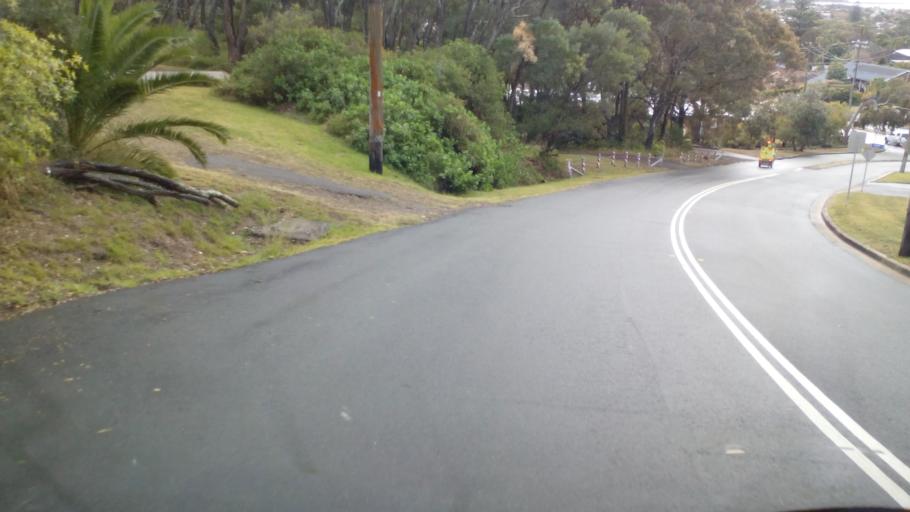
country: AU
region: New South Wales
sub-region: Lake Macquarie Shire
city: Belmont South
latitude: -33.1084
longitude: 151.6400
